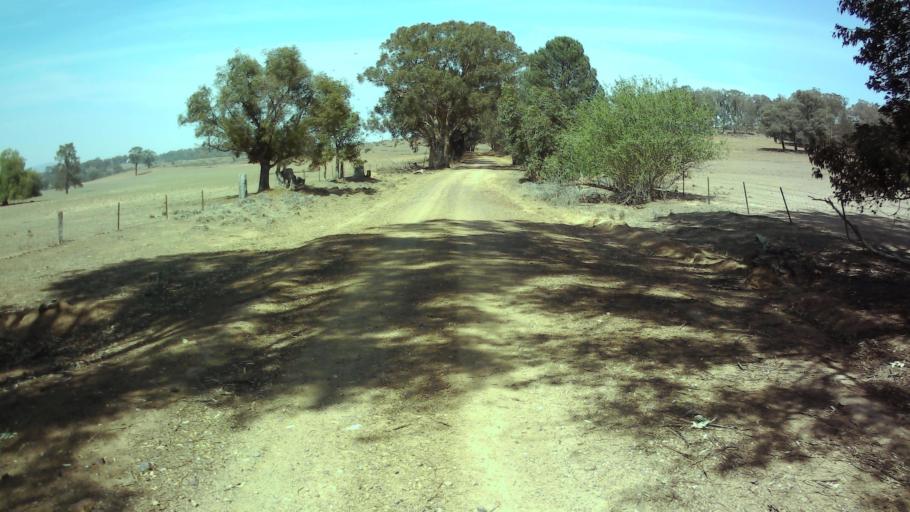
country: AU
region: New South Wales
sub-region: Weddin
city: Grenfell
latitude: -33.8966
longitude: 148.1352
